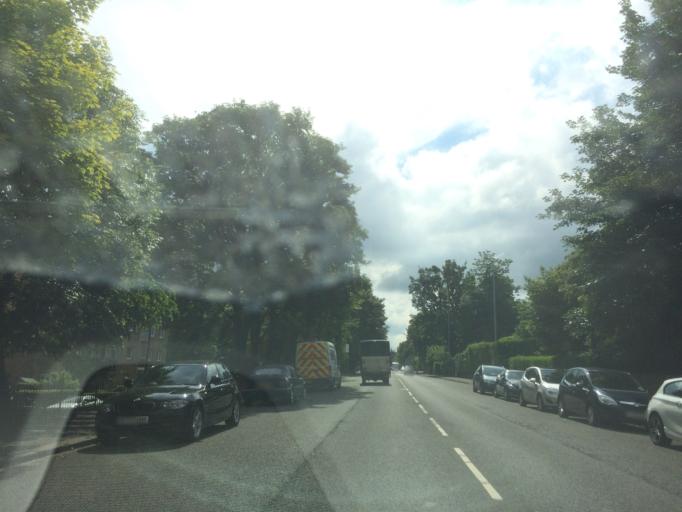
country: GB
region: Scotland
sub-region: East Renfrewshire
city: Giffnock
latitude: 55.8173
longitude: -4.2912
